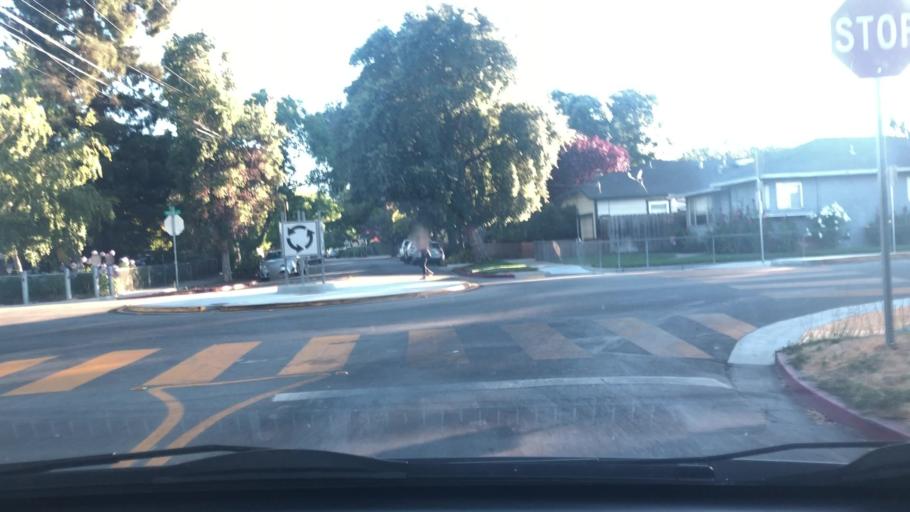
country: US
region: California
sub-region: San Mateo County
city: Redwood City
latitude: 37.4767
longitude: -122.2352
